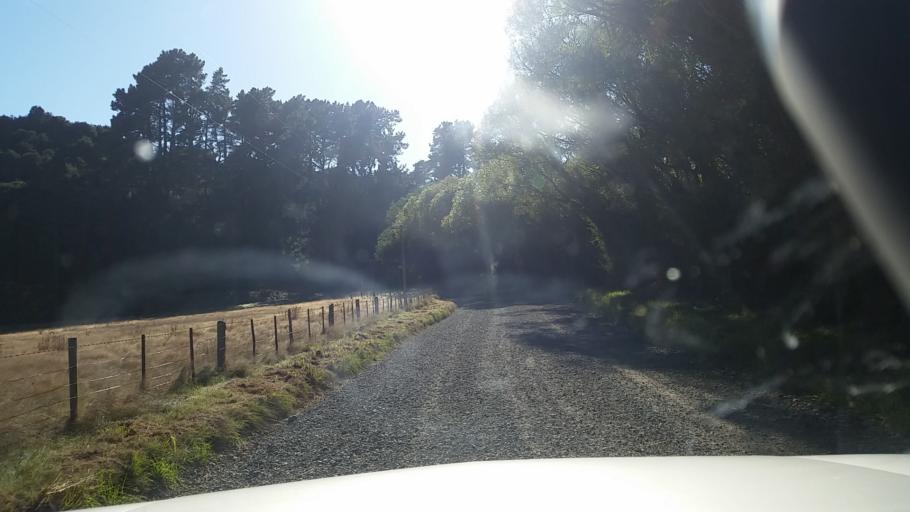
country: NZ
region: Marlborough
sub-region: Marlborough District
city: Blenheim
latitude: -41.4514
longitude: 173.8716
